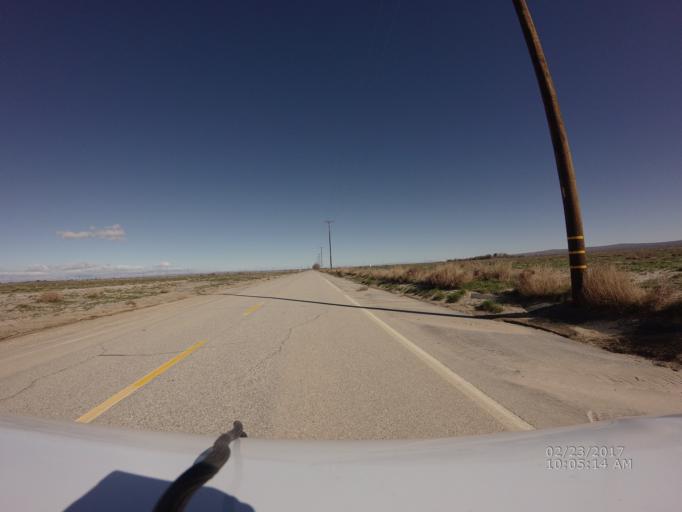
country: US
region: California
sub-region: Los Angeles County
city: Lake Los Angeles
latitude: 34.6846
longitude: -117.9342
